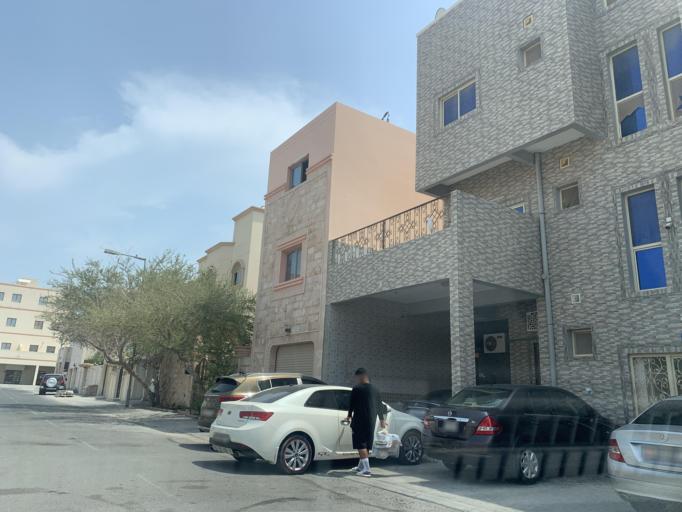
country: BH
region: Muharraq
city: Al Hadd
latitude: 26.2738
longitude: 50.6558
